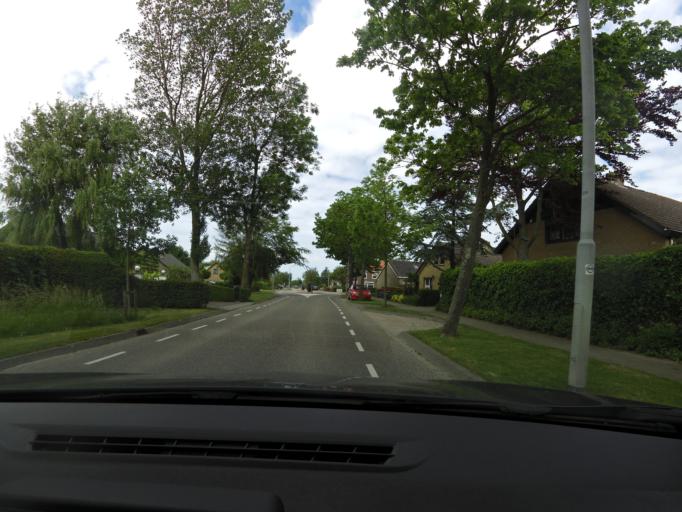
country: NL
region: Zeeland
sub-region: Schouwen-Duiveland
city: Scharendijke
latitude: 51.7337
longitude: 3.8408
